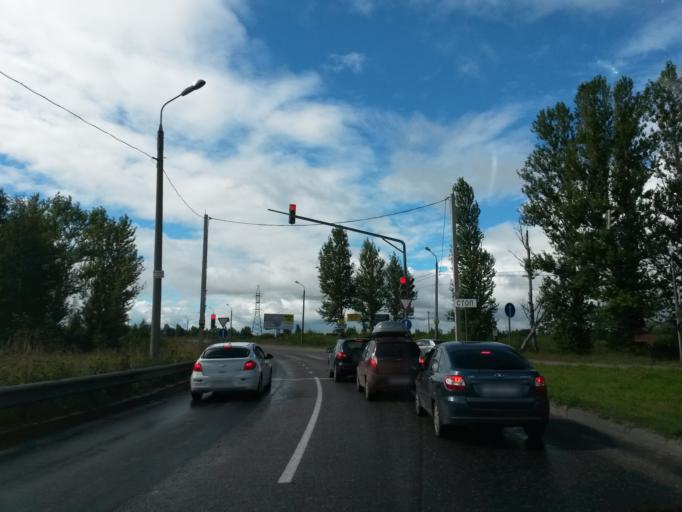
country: RU
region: Jaroslavl
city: Yaroslavl
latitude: 57.6719
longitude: 39.7714
